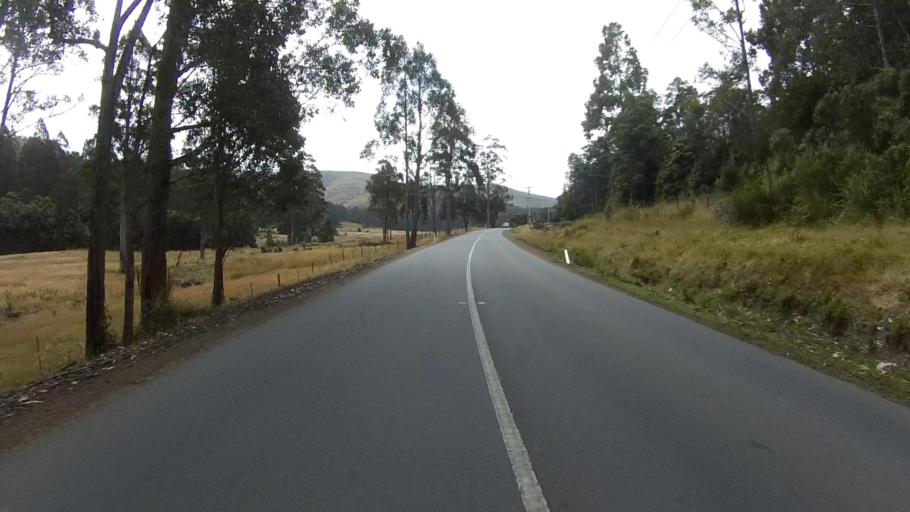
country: AU
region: Tasmania
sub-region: Kingborough
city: Kettering
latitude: -43.1223
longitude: 147.1845
